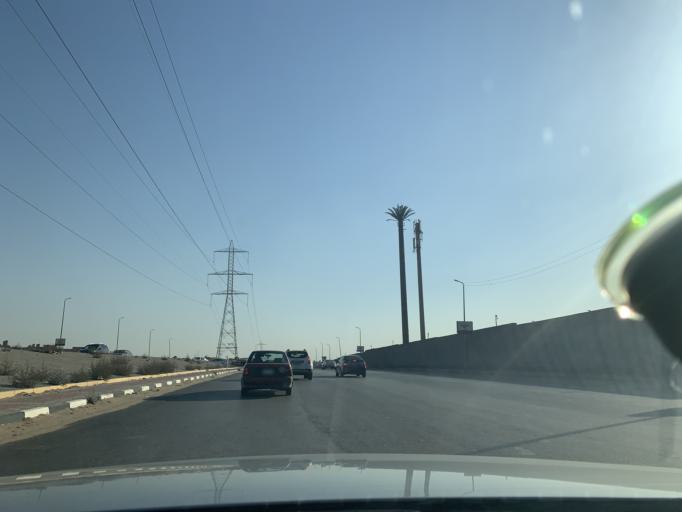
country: EG
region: Muhafazat al Qahirah
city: Cairo
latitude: 30.0347
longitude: 31.3521
